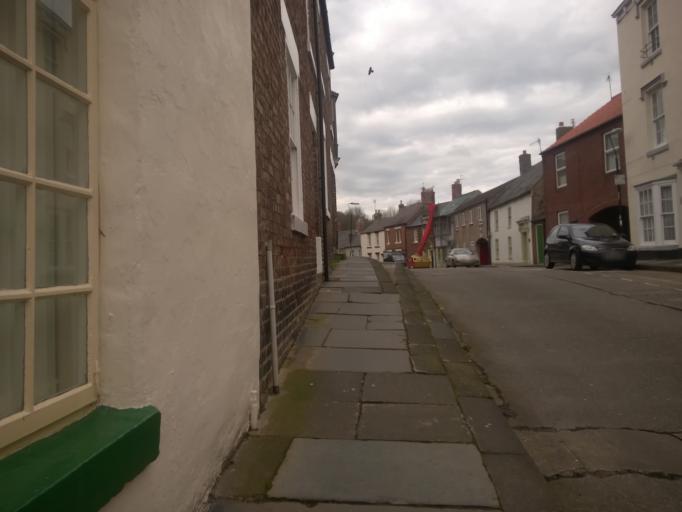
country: GB
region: England
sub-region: County Durham
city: Durham
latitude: 54.7762
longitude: -1.5819
